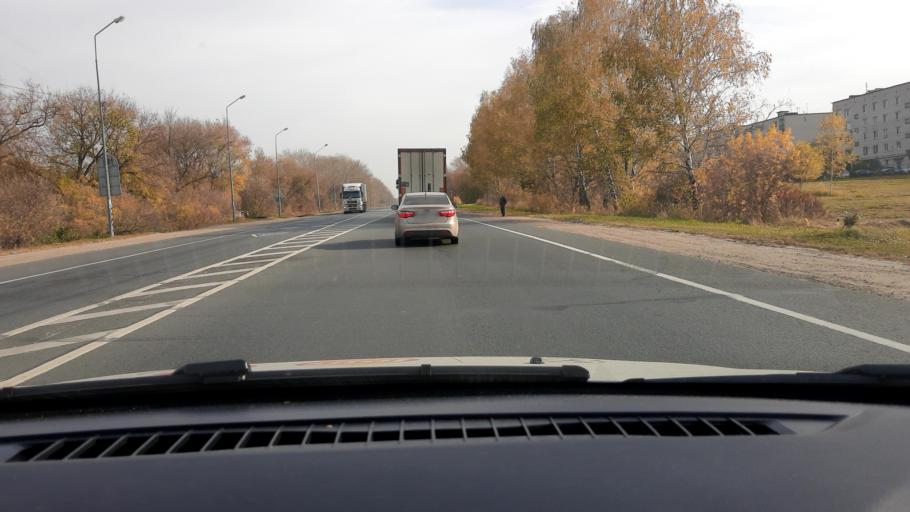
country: RU
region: Nizjnij Novgorod
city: Pamyat' Parizhskoy Kommuny
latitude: 56.0423
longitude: 44.4449
